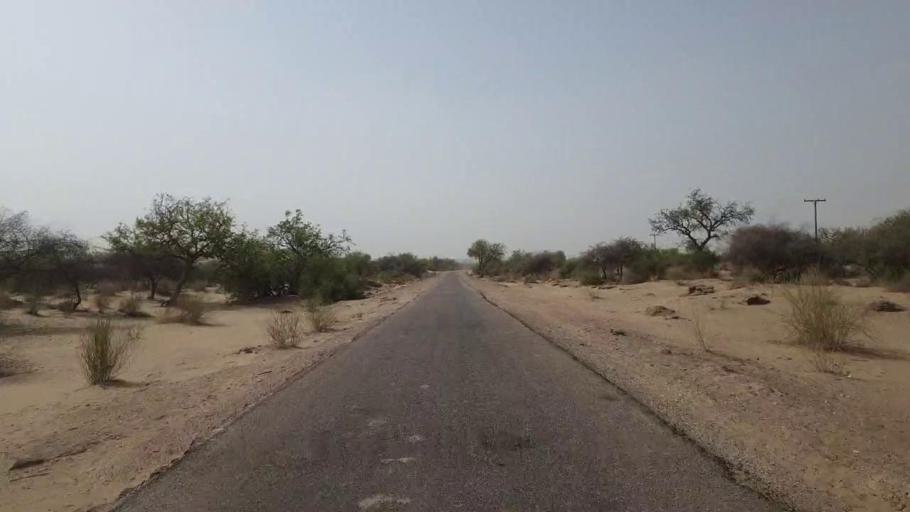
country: PK
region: Sindh
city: Mithi
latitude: 24.6031
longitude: 69.9227
